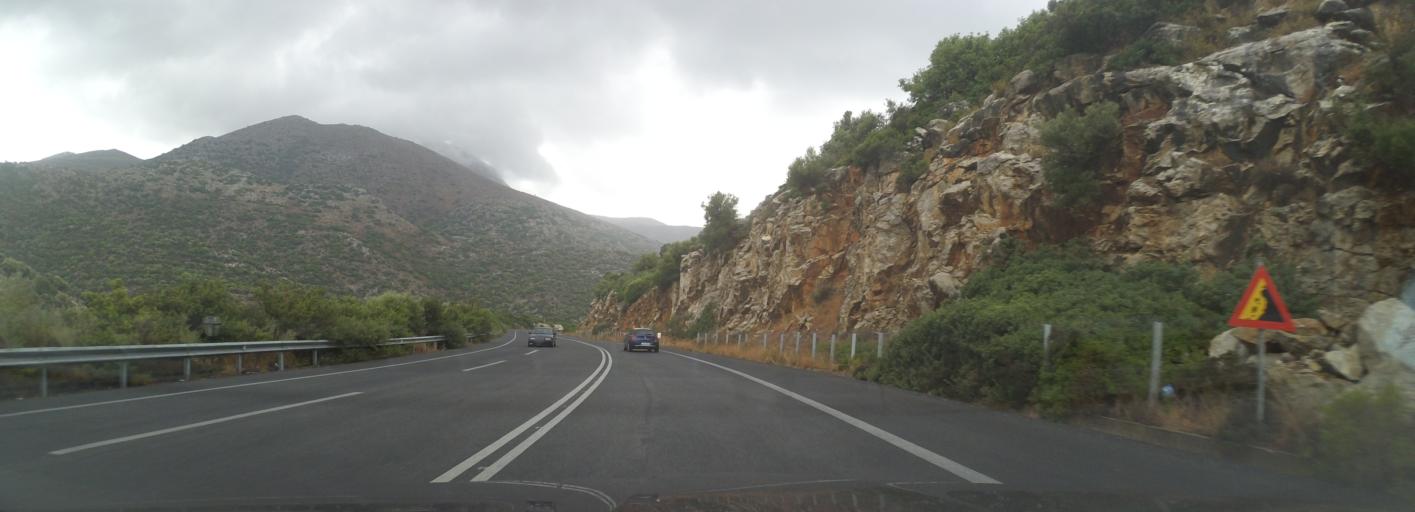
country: GR
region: Crete
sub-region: Nomos Irakleiou
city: Tilisos
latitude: 35.4029
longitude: 24.9817
